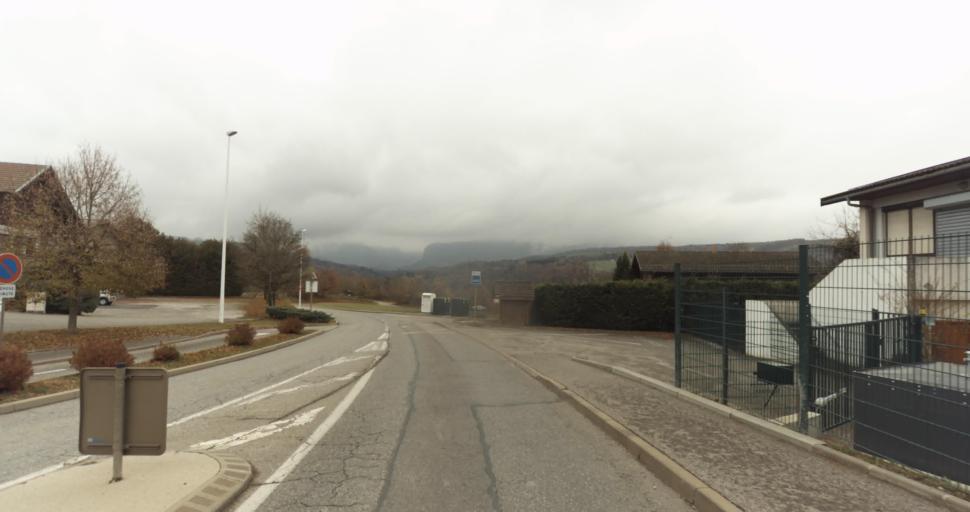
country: FR
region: Rhone-Alpes
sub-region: Departement de la Haute-Savoie
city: Groisy
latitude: 46.0053
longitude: 6.1774
